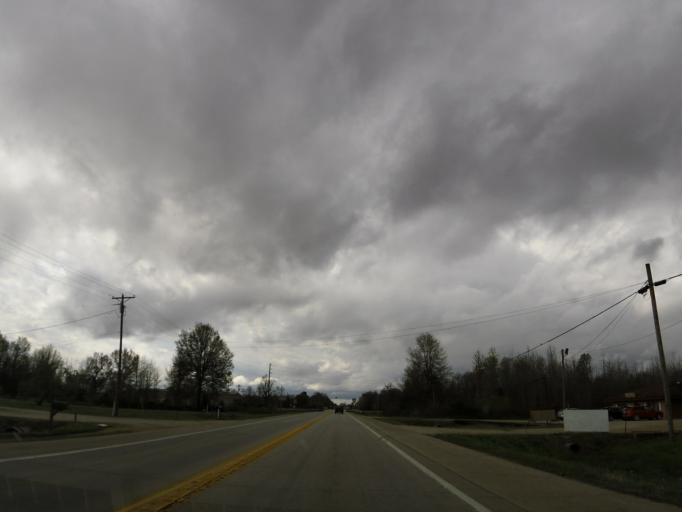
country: US
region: Arkansas
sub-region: Clay County
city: Corning
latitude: 36.5640
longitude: -90.5210
